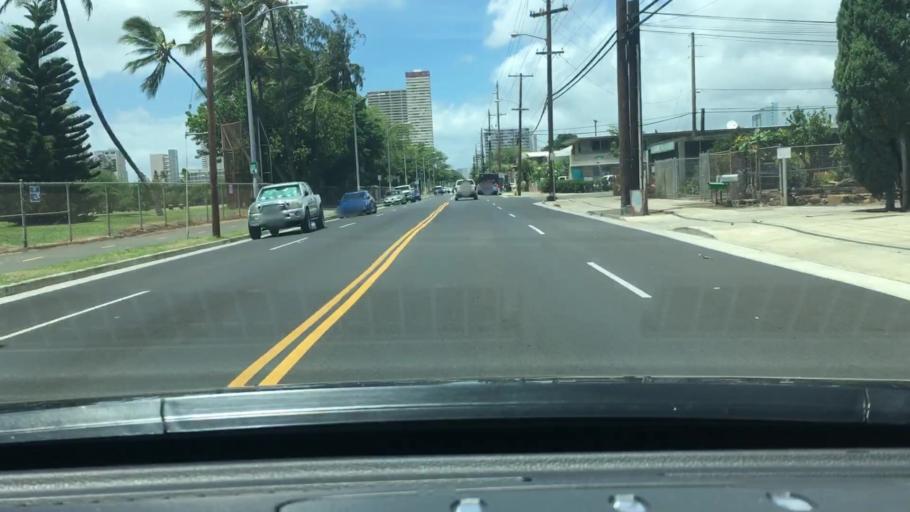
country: US
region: Hawaii
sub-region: Honolulu County
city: Honolulu
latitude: 21.2818
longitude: -157.8170
